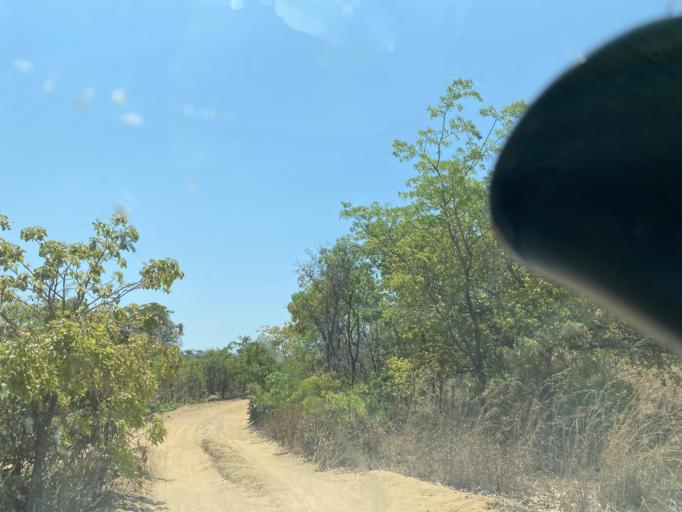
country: ZM
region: Lusaka
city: Chongwe
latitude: -15.4392
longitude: 29.2023
